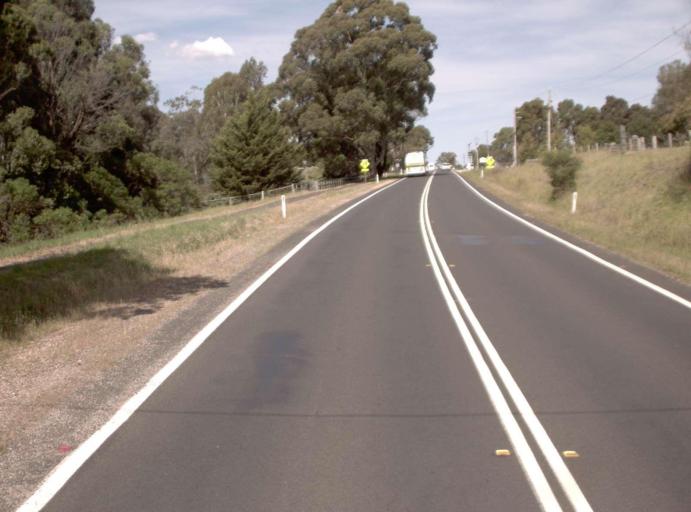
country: AU
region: Victoria
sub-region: East Gippsland
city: Bairnsdale
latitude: -37.8153
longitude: 147.7437
